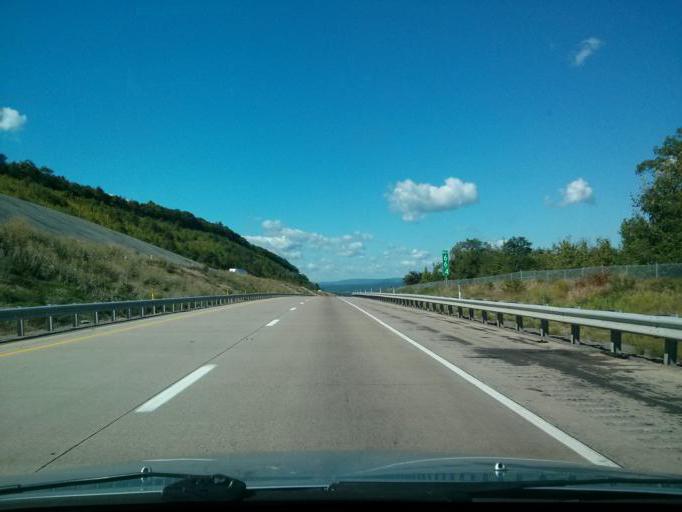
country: US
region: Pennsylvania
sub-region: Centre County
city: Stormstown
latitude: 40.8323
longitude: -77.9812
